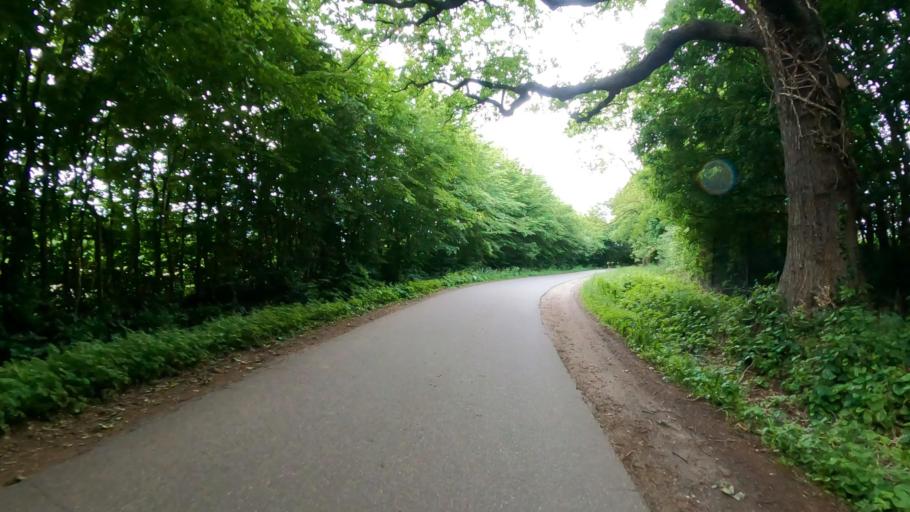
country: DE
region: Schleswig-Holstein
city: Rellingen
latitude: 53.6389
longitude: 9.8313
